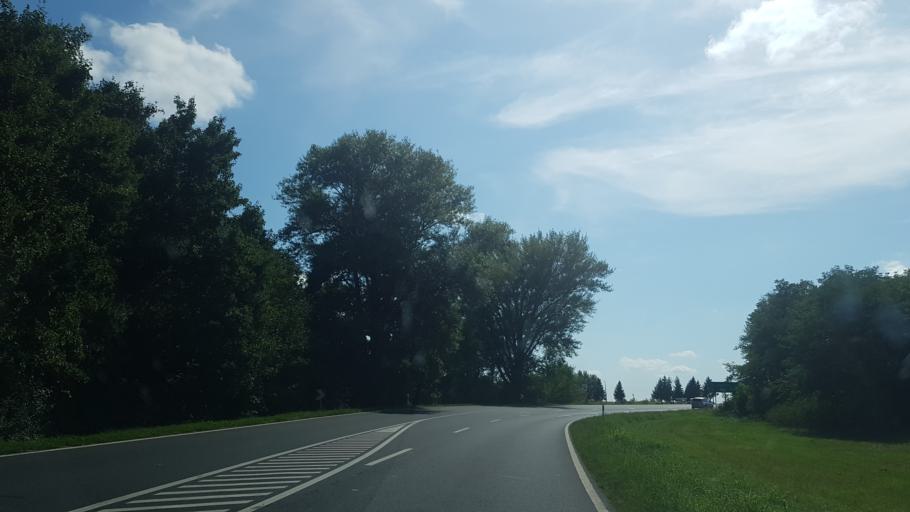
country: HU
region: Somogy
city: Bohonye
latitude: 46.4004
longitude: 17.3858
